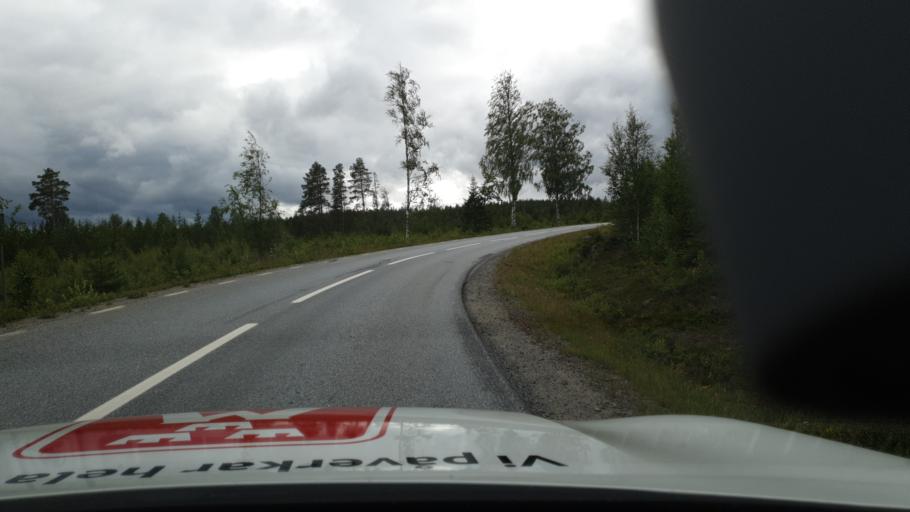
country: SE
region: Vaesterbotten
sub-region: Skelleftea Kommun
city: Burtraesk
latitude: 64.4026
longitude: 20.3829
